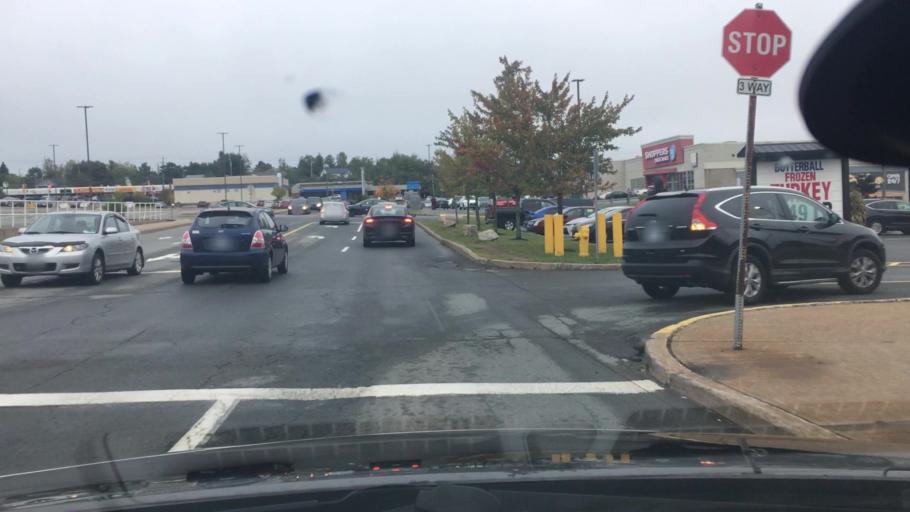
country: CA
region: Nova Scotia
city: Dartmouth
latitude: 44.7724
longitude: -63.6953
